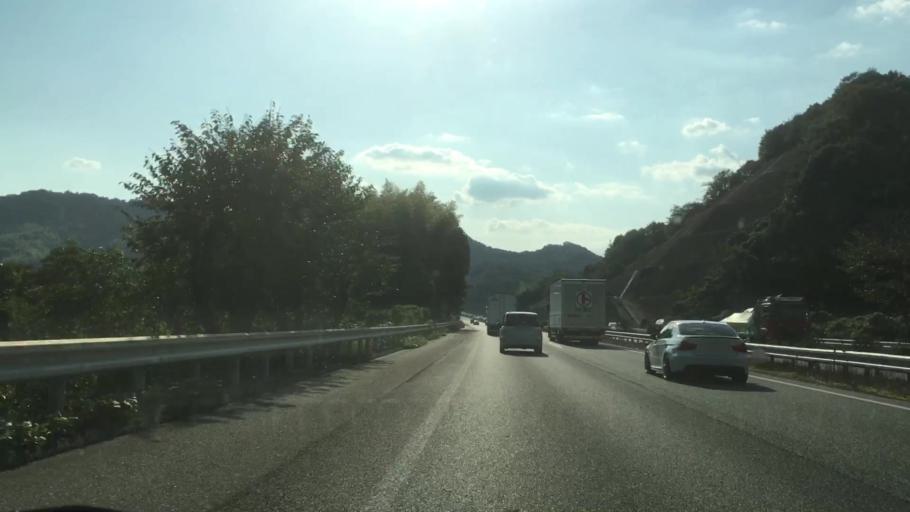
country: JP
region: Yamaguchi
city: Tokuyama
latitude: 34.0806
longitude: 131.7271
